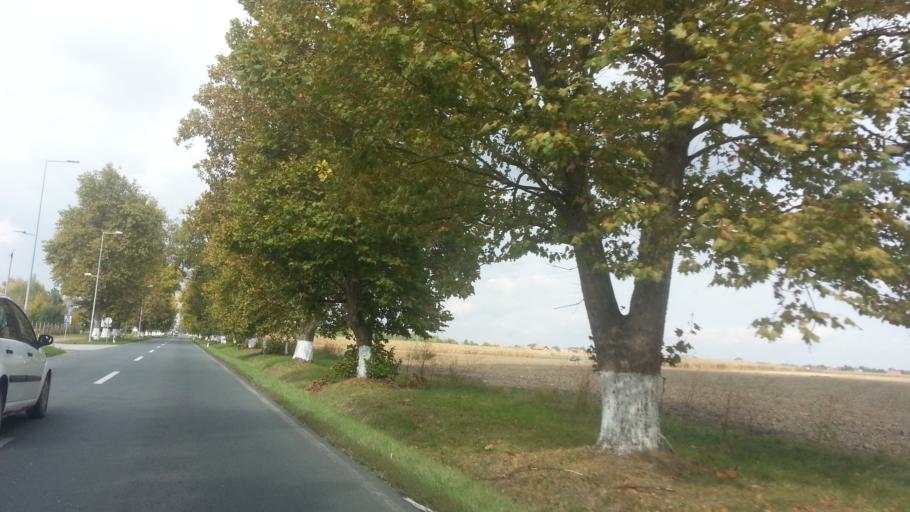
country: RS
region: Autonomna Pokrajina Vojvodina
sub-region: Sremski Okrug
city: Stara Pazova
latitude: 44.9711
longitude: 20.1767
